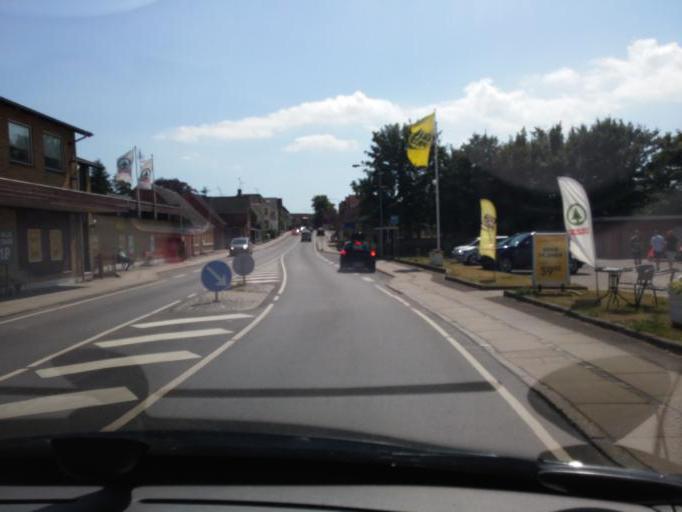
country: DK
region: South Denmark
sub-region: Langeland Kommune
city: Rudkobing
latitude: 54.8286
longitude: 10.6998
